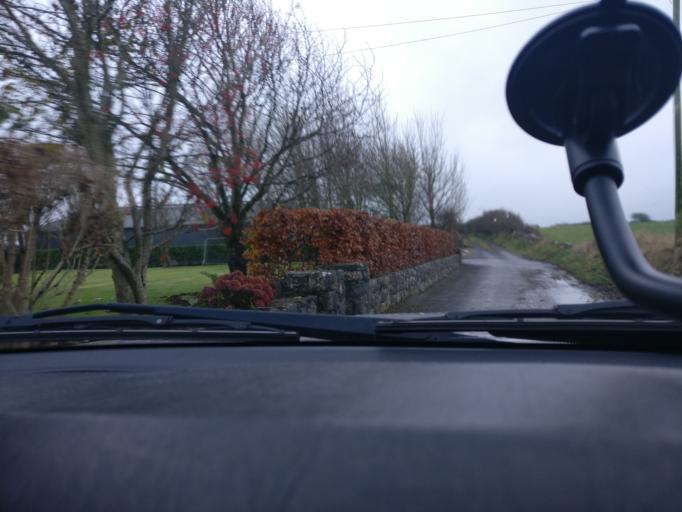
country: IE
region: Connaught
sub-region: County Galway
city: Loughrea
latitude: 53.2127
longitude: -8.5471
